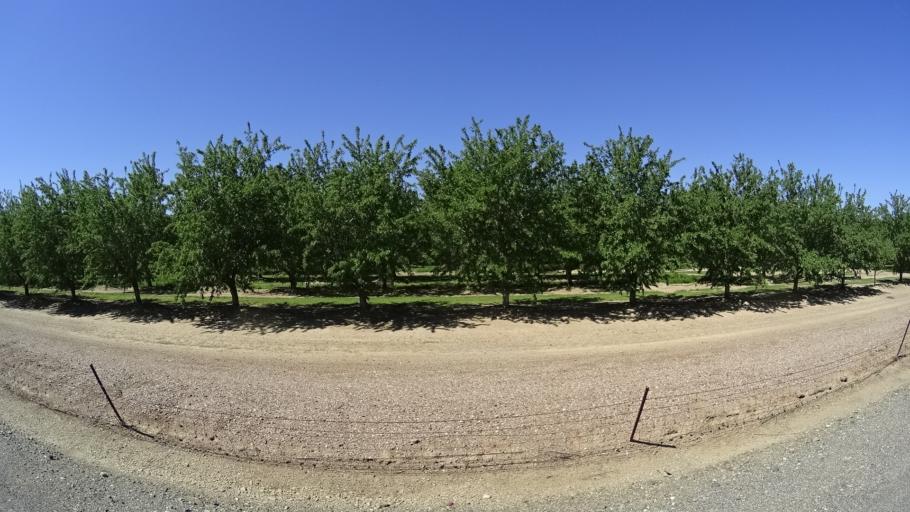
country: US
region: California
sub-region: Glenn County
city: Orland
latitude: 39.6605
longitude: -122.2346
